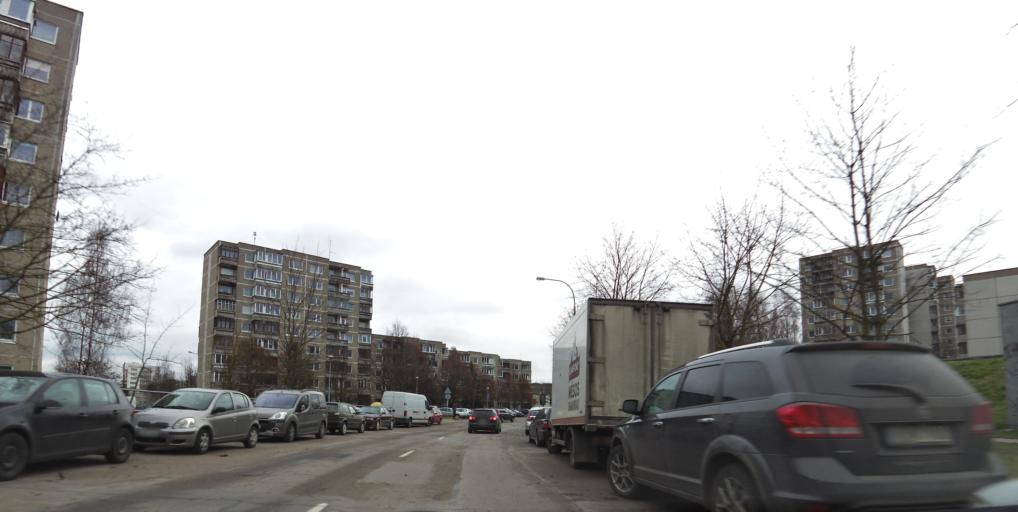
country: LT
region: Vilnius County
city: Justiniskes
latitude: 54.7205
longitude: 25.2281
